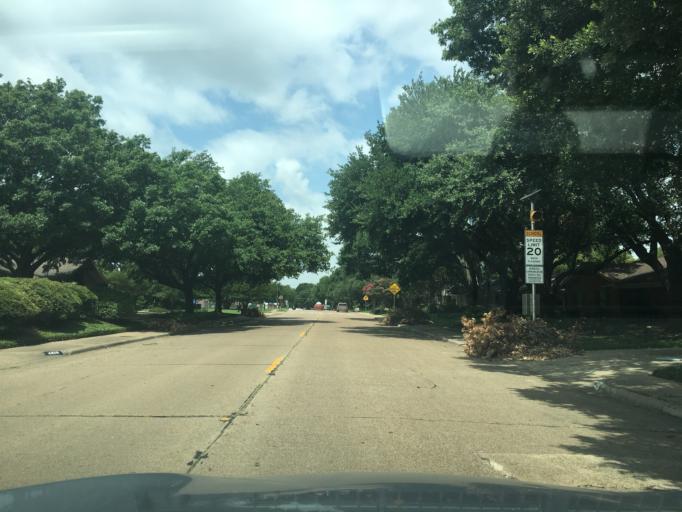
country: US
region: Texas
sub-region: Dallas County
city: Addison
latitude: 32.9224
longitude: -96.8255
